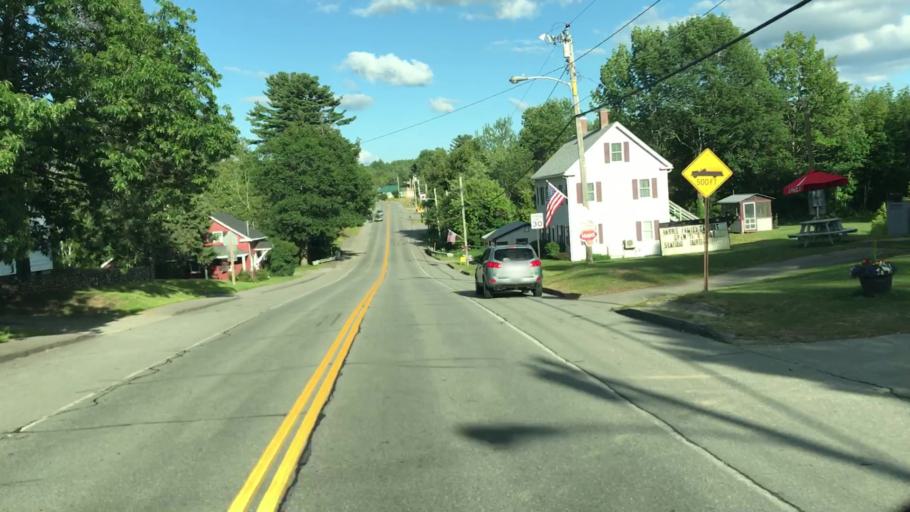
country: US
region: Maine
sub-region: Penobscot County
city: Lincoln
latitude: 45.3599
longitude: -68.2855
